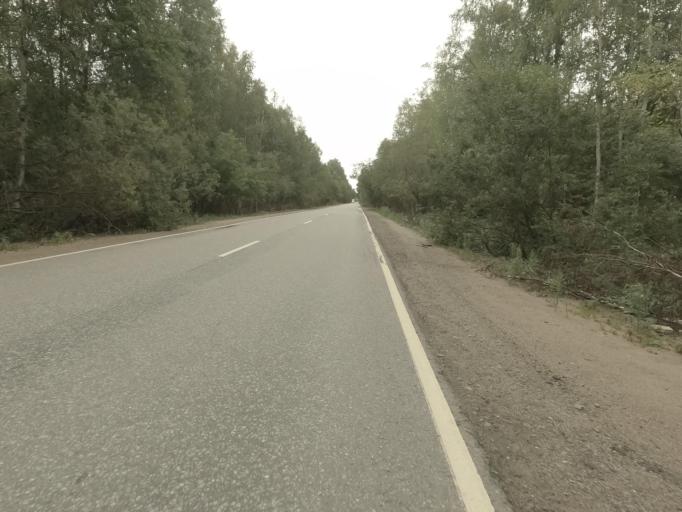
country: RU
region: Leningrad
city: Koltushi
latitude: 59.8999
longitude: 30.7655
